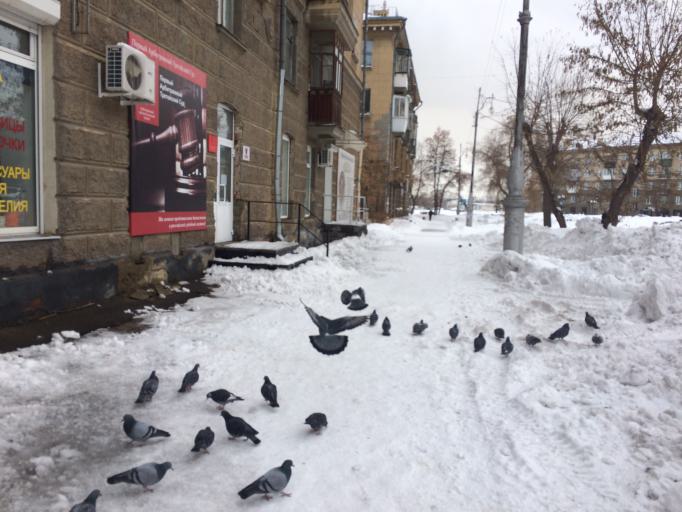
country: RU
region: Chelyabinsk
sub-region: Gorod Magnitogorsk
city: Magnitogorsk
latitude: 53.4189
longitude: 58.9995
